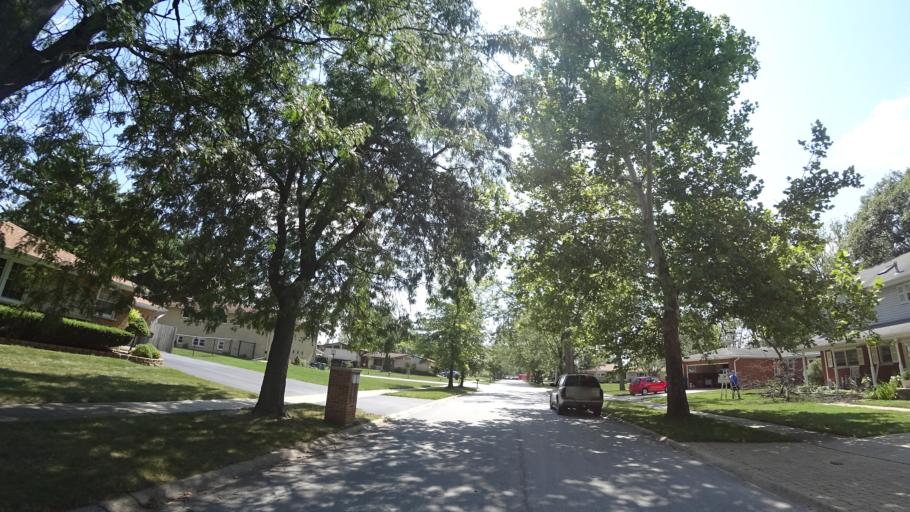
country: US
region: Illinois
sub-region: Cook County
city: Orland Park
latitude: 41.6293
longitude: -87.8275
